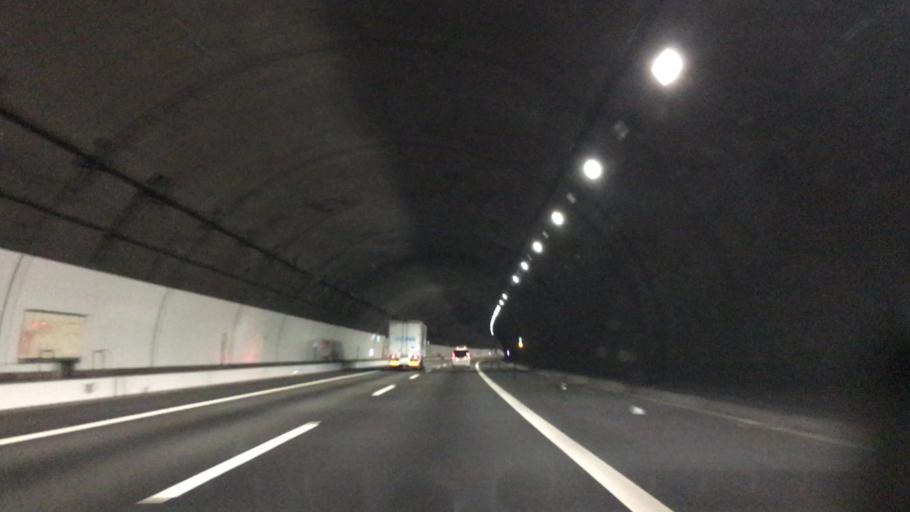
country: JP
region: Shiga Prefecture
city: Kusatsu
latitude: 34.9512
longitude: 136.0181
